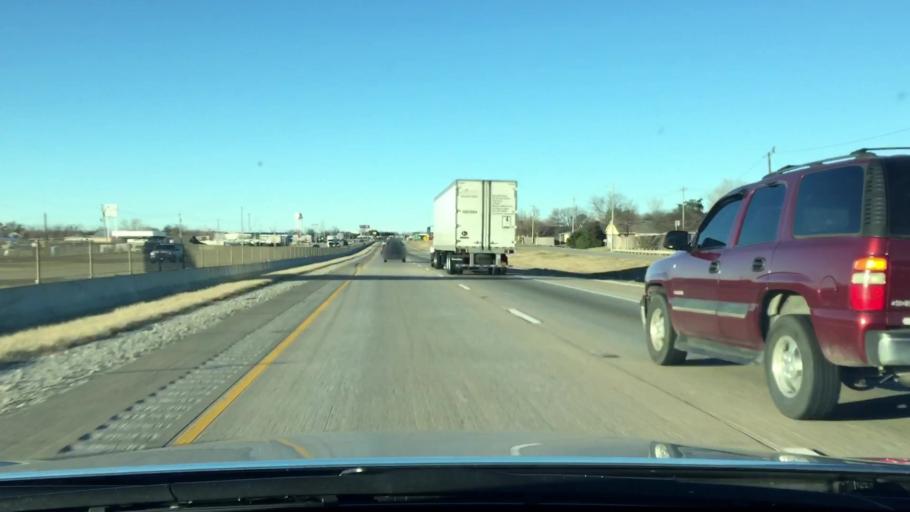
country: US
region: Texas
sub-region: Denton County
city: Sanger
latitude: 33.3510
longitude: -97.1820
